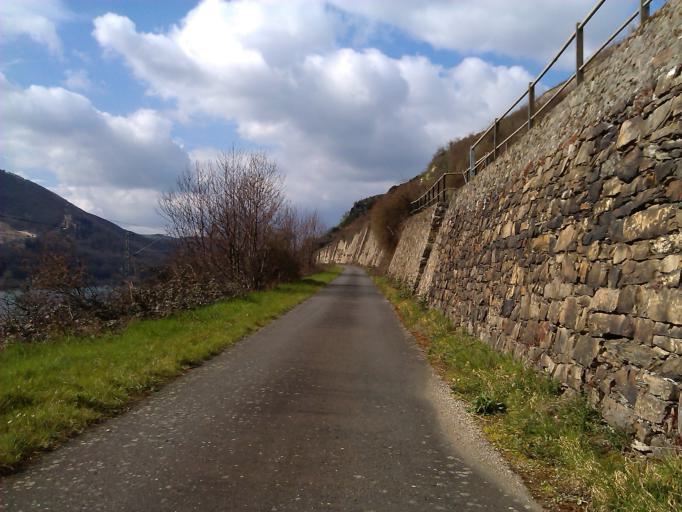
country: DE
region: Rheinland-Pfalz
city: Trechtingshausen
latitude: 50.0175
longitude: 7.8481
